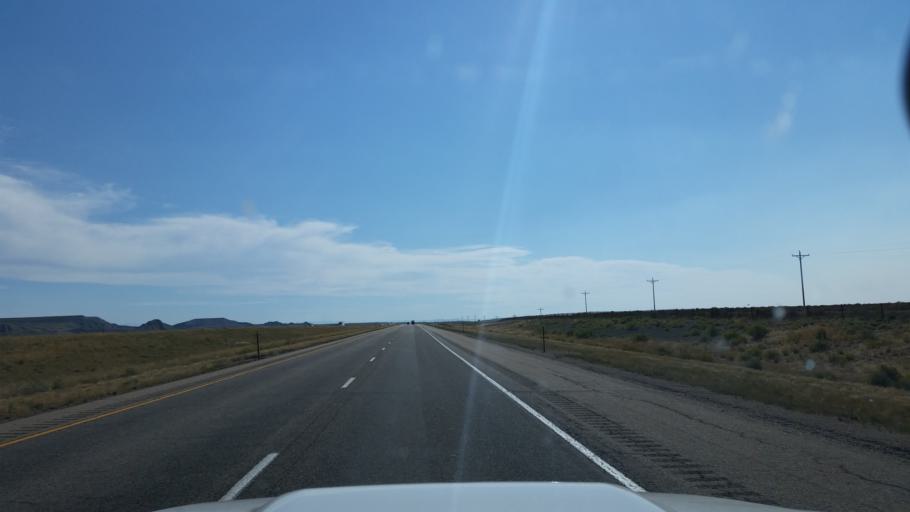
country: US
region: Wyoming
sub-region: Uinta County
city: Lyman
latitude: 41.4495
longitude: -110.0763
